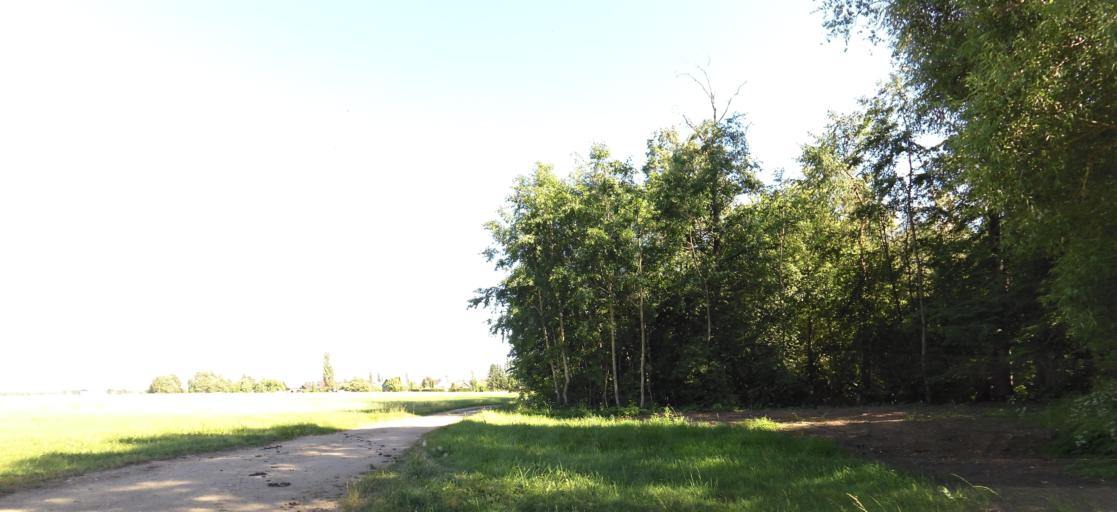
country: LT
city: Vabalninkas
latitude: 56.0250
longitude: 24.7131
